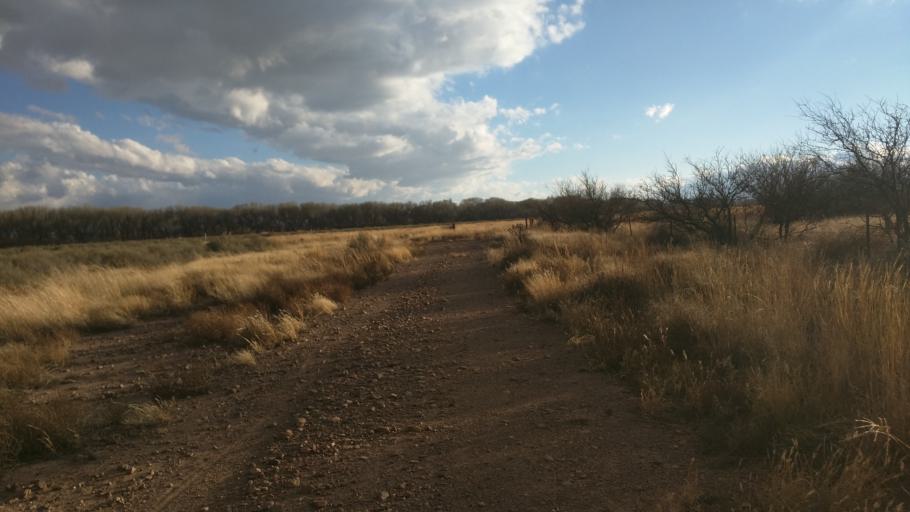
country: US
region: Arizona
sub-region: Cochise County
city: Sierra Vista Southeast
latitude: 31.3698
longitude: -110.1223
